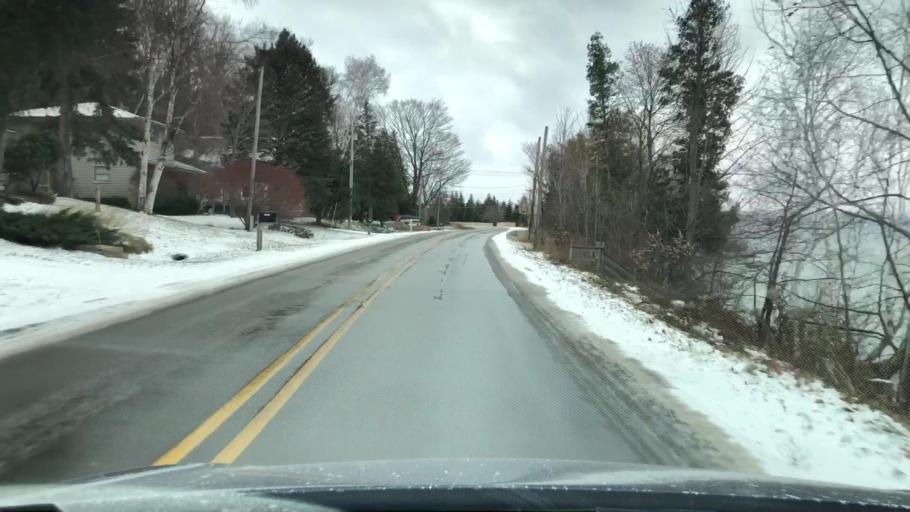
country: US
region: Michigan
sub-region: Leelanau County
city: Greilickville
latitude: 44.8398
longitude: -85.5601
